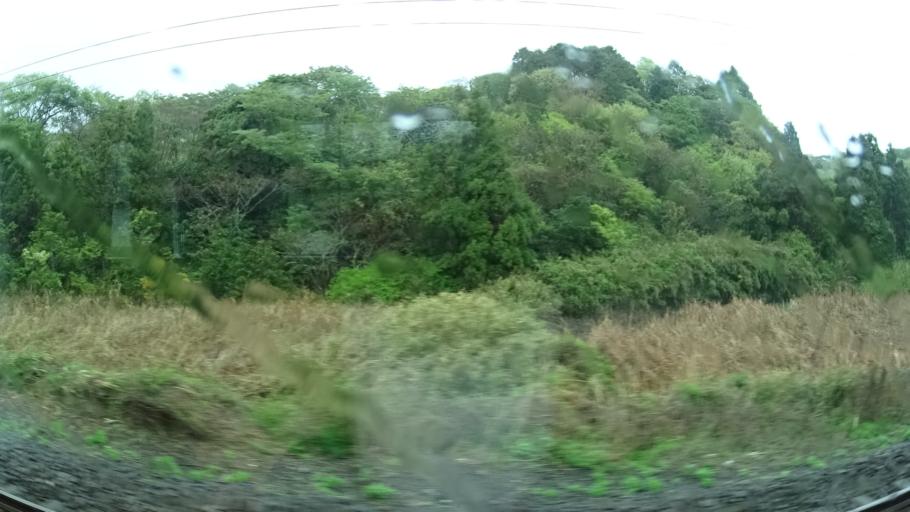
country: JP
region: Ibaraki
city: Kitaibaraki
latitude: 36.8128
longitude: 140.7639
